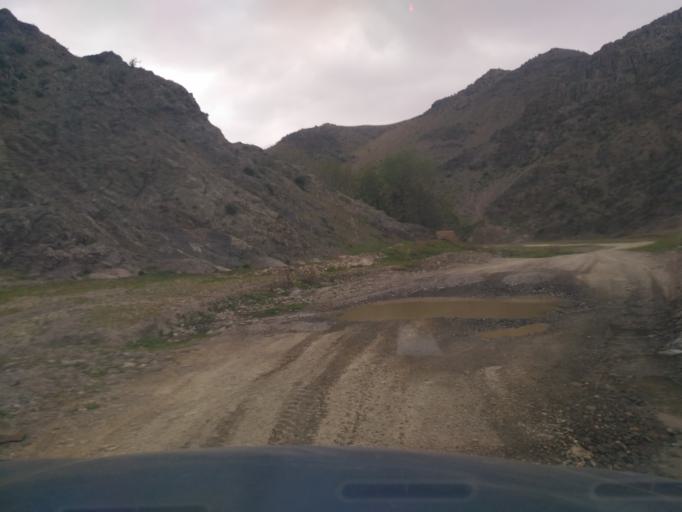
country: UZ
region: Jizzax
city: Zomin
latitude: 39.8510
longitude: 68.3956
